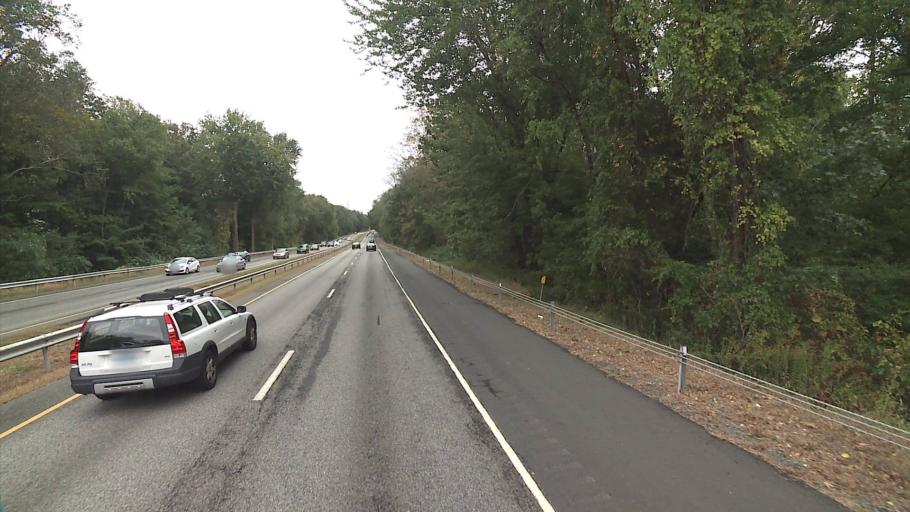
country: US
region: Connecticut
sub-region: New Haven County
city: Wallingford Center
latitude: 41.4339
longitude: -72.8508
